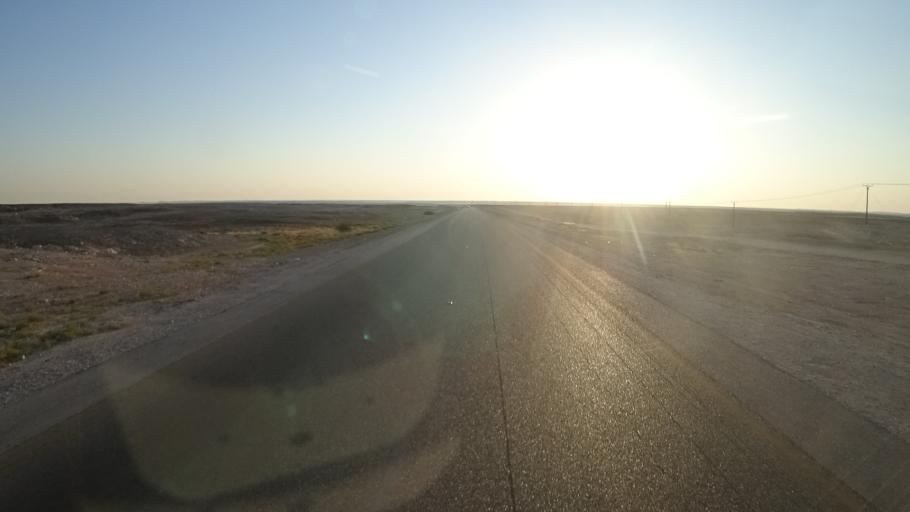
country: OM
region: Zufar
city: Salalah
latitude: 17.5373
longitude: 53.4103
